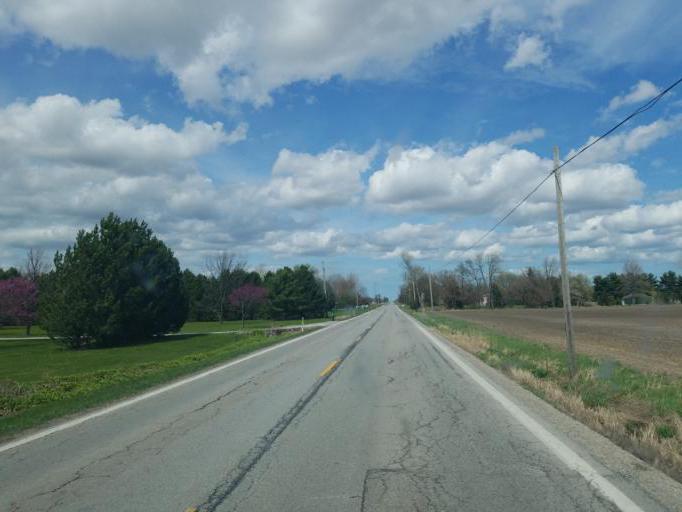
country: US
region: Ohio
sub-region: Huron County
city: Bellevue
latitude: 41.2702
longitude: -82.7925
